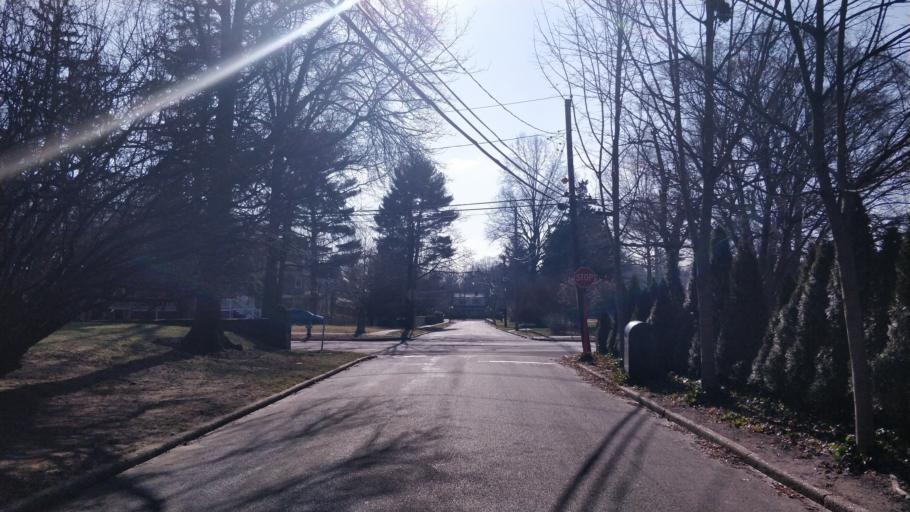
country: US
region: New York
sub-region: Nassau County
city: Sea Cliff
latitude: 40.8503
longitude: -73.6387
